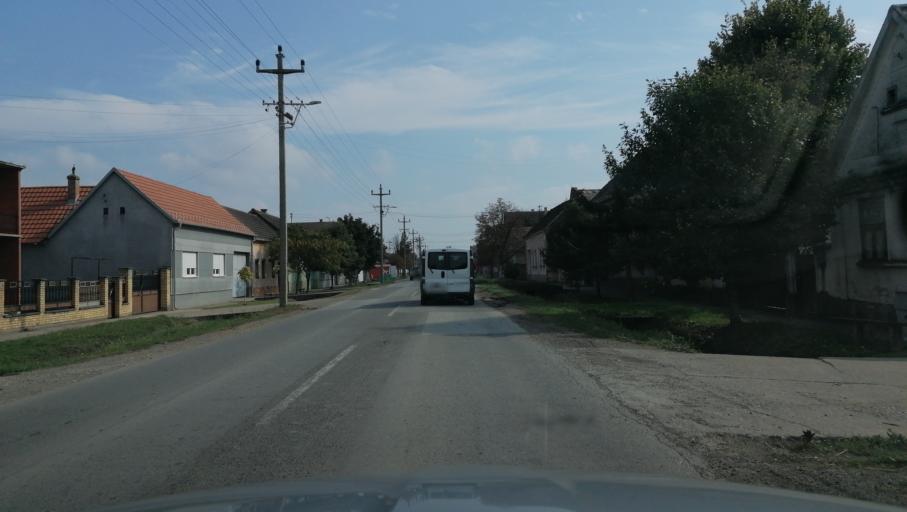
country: RS
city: Ravnje
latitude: 45.0239
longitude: 19.4006
